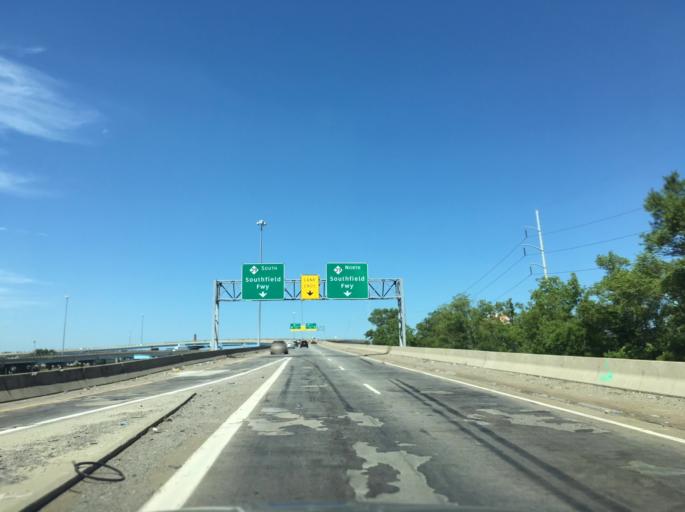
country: US
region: Michigan
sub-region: Wayne County
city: Dearborn
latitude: 42.3794
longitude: -83.2118
